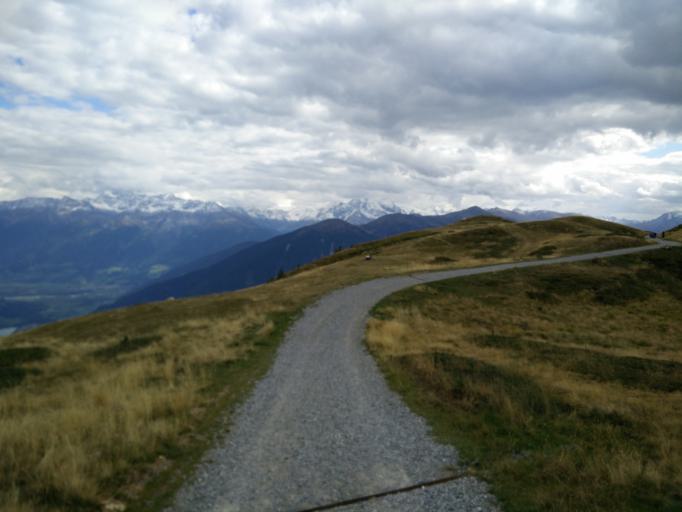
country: IT
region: Trentino-Alto Adige
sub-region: Bolzano
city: Malles Venosta
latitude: 46.7138
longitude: 10.4965
